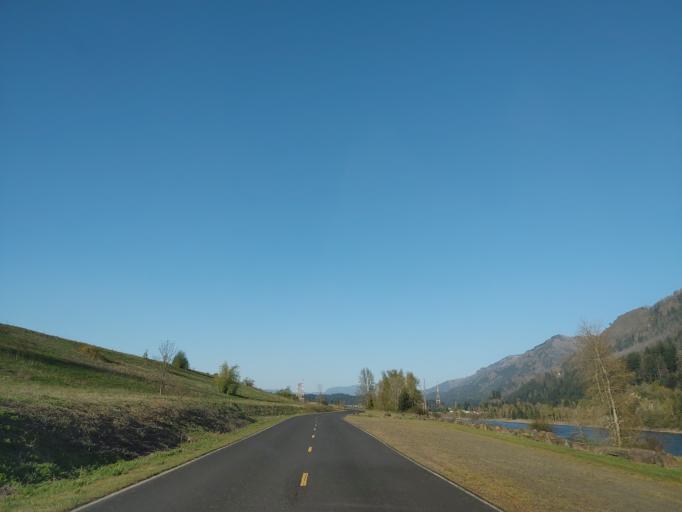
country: US
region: Oregon
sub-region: Hood River County
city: Cascade Locks
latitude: 45.6291
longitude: -121.9753
